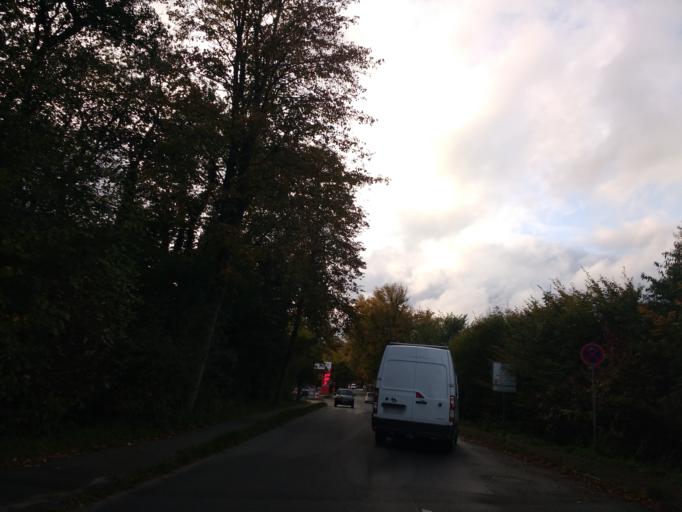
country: DE
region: Schleswig-Holstein
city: Schonwalde am Bungsberg
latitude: 54.1872
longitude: 10.7599
